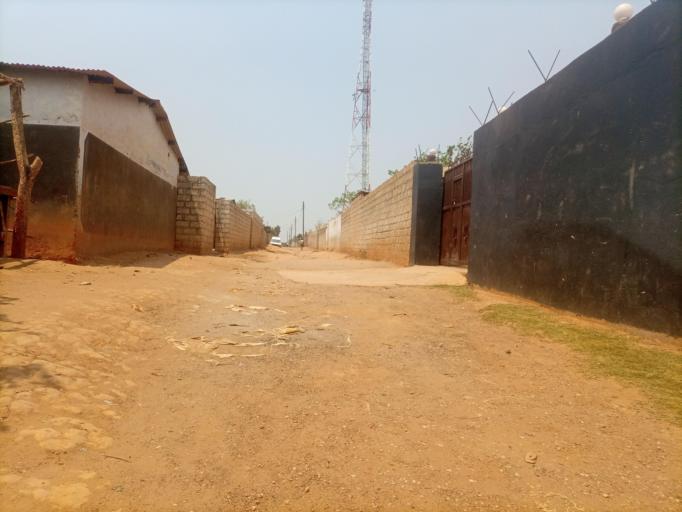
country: ZM
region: Lusaka
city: Lusaka
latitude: -15.3945
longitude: 28.3793
